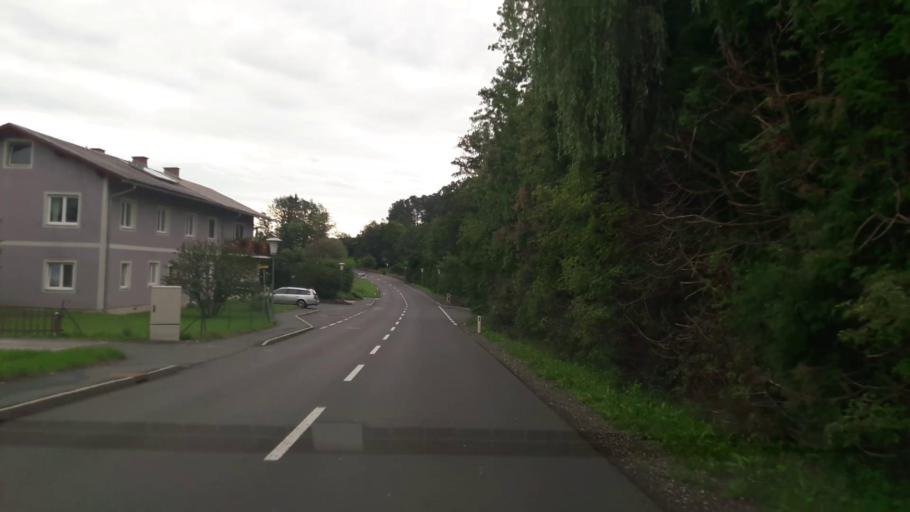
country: AT
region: Styria
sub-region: Politischer Bezirk Hartberg-Fuerstenfeld
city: Dienersdorf
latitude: 47.2226
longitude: 15.8561
